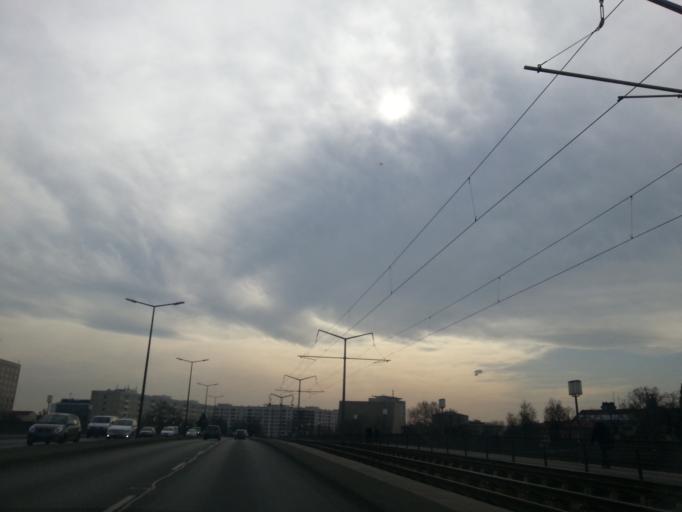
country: DE
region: Saxony
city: Dresden
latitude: 51.0553
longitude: 13.7467
